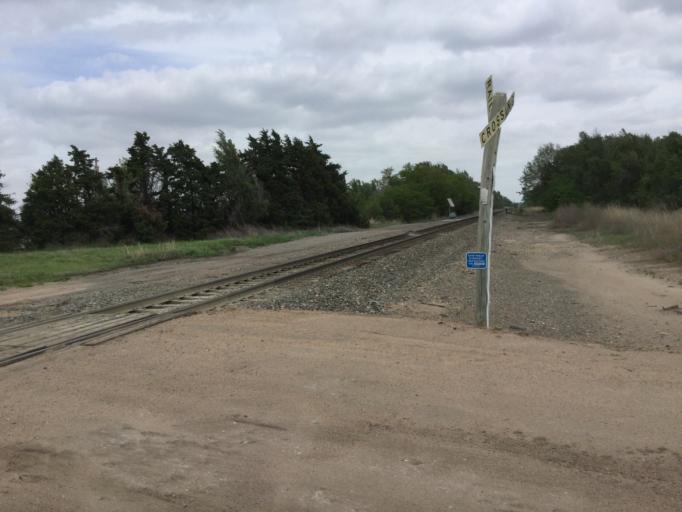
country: US
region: Kansas
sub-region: Edwards County
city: Kinsley
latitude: 37.9274
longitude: -99.4051
